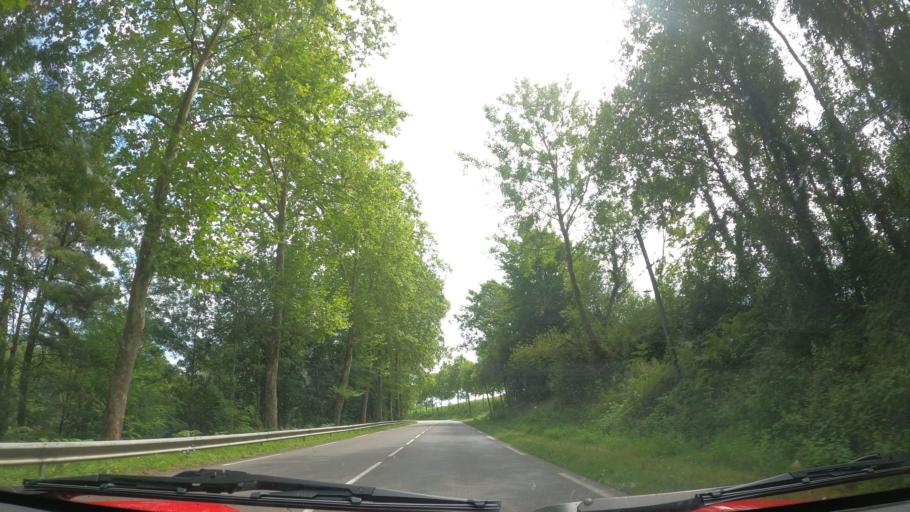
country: FR
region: Aquitaine
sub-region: Departement des Landes
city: Peyrehorade
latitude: 43.5287
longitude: -1.1055
